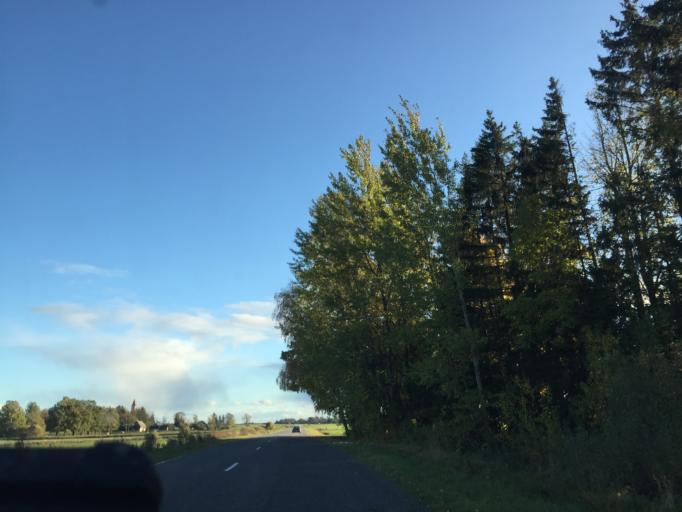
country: LV
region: Saldus Rajons
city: Saldus
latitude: 56.8185
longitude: 22.3784
